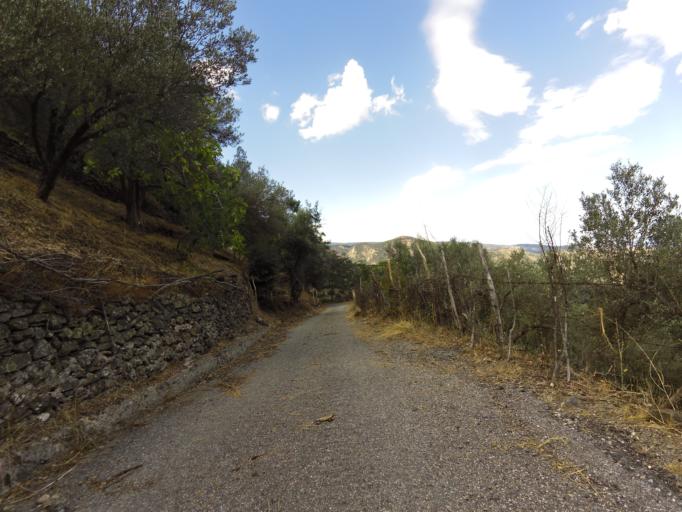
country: IT
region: Calabria
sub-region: Provincia di Reggio Calabria
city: Pazzano
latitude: 38.4705
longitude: 16.4287
